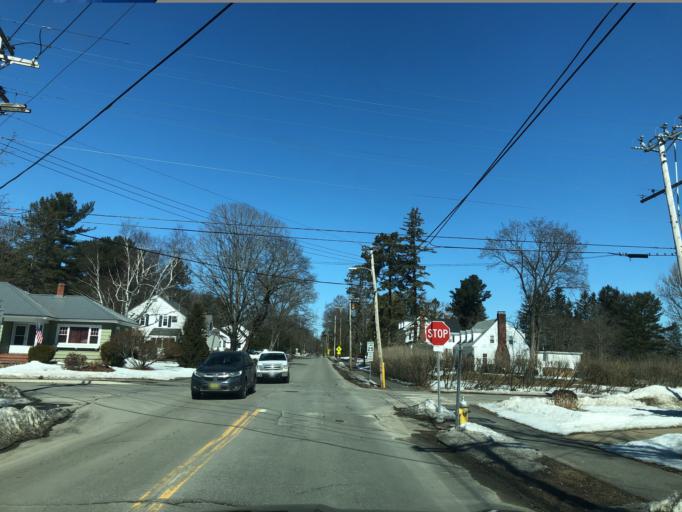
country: US
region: Maine
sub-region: Penobscot County
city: Brewer
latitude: 44.8106
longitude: -68.7523
